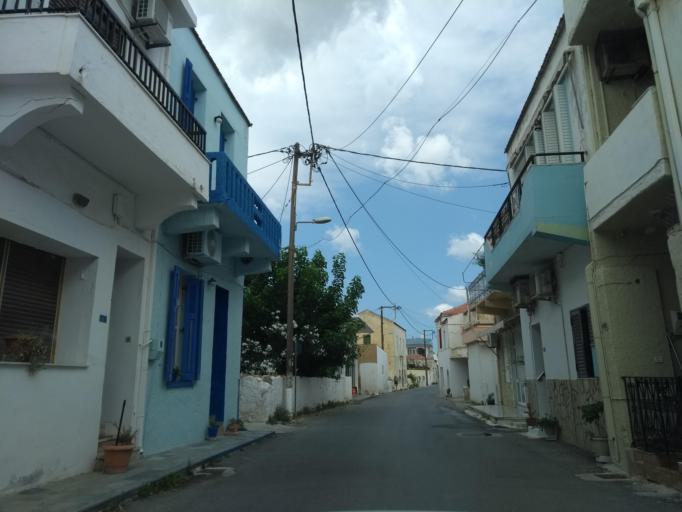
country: GR
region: Crete
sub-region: Nomos Chanias
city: Kalivai
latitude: 35.4546
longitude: 24.1706
